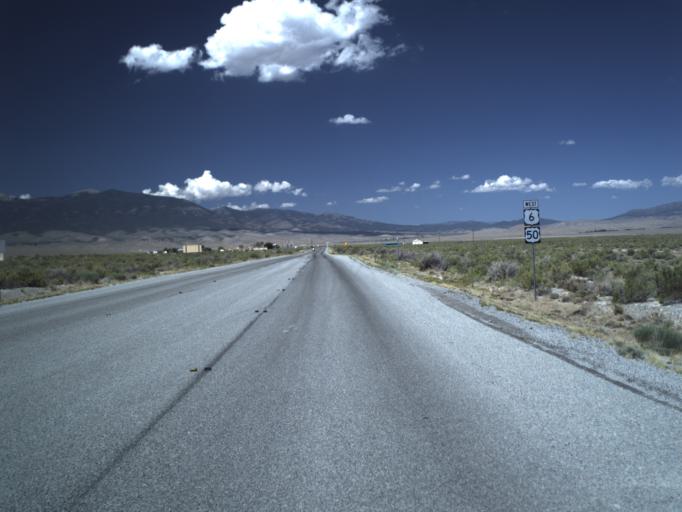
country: US
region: Nevada
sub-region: White Pine County
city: McGill
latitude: 39.0563
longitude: -114.0369
